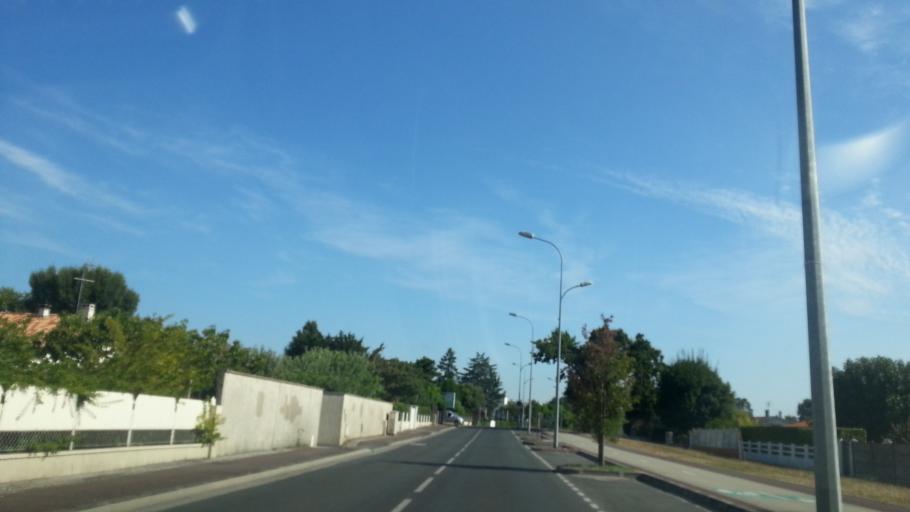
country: FR
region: Aquitaine
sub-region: Departement de la Gironde
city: Leognan
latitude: 44.7606
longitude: -0.5823
